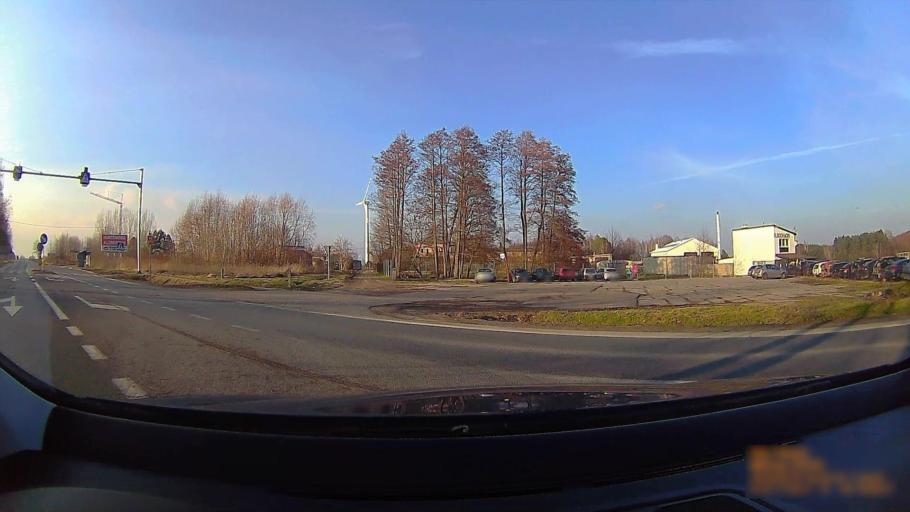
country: PL
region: Greater Poland Voivodeship
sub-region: Konin
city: Konin
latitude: 52.1906
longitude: 18.3327
